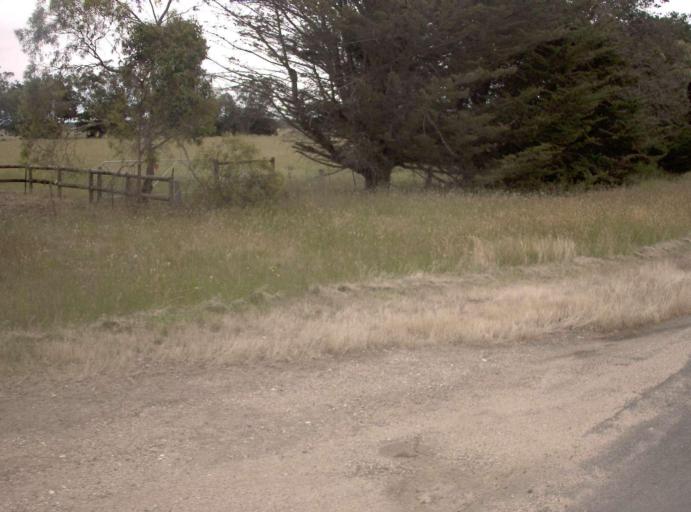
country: AU
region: Victoria
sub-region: Wellington
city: Sale
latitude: -38.2815
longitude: 147.0372
